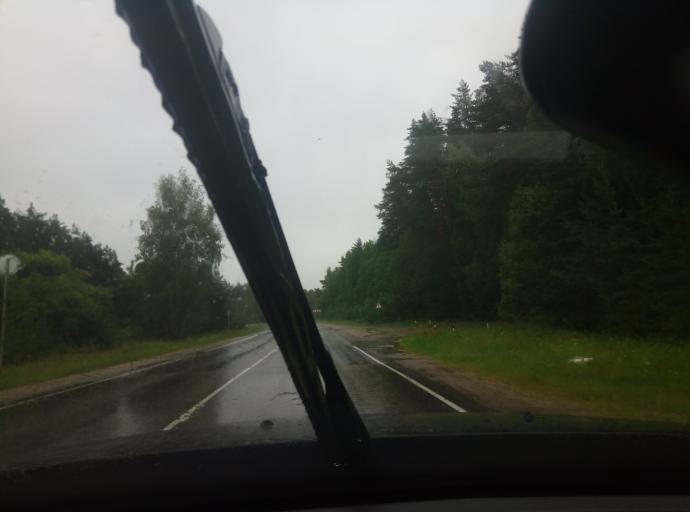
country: RU
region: Kaluga
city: Kremenki
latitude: 54.8792
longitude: 37.1636
